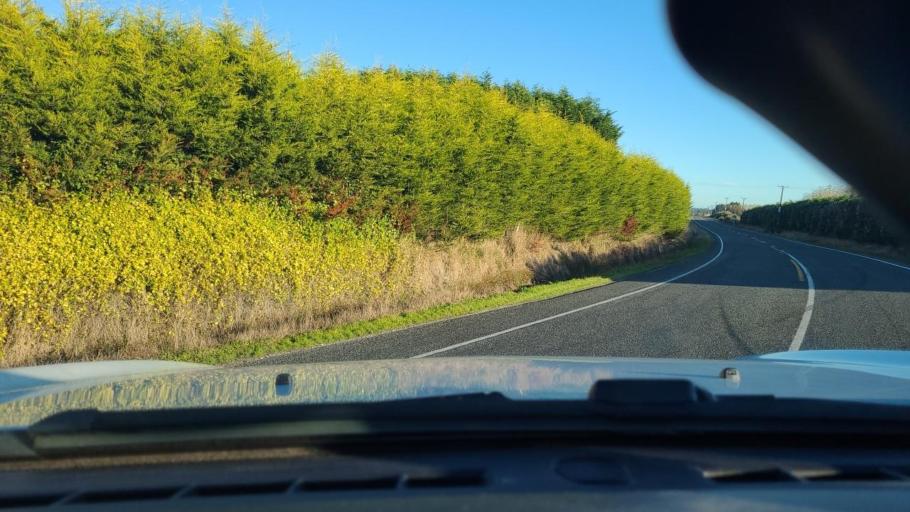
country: NZ
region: Southland
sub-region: Invercargill City
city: Invercargill
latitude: -46.4053
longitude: 168.5520
